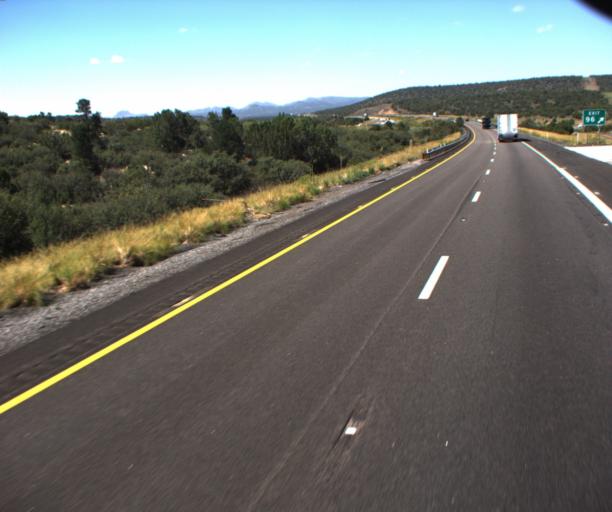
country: US
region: Arizona
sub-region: Mohave County
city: Peach Springs
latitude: 35.2072
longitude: -113.2945
